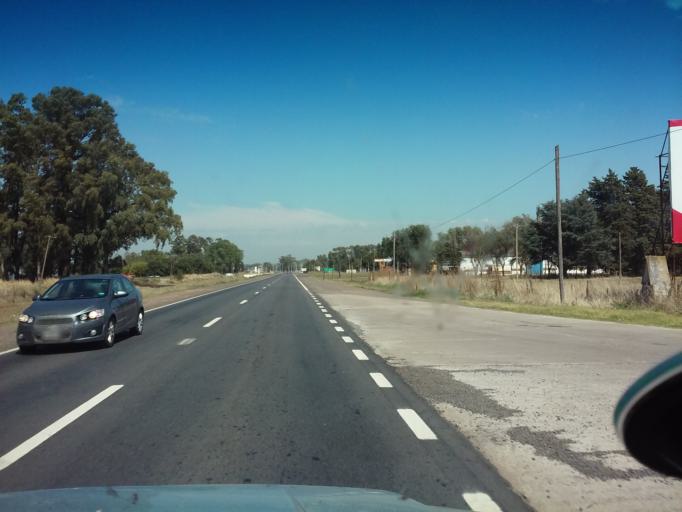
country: AR
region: Buenos Aires
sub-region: Partido de Nueve de Julio
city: Nueve de Julio
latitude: -35.4628
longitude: -60.8407
